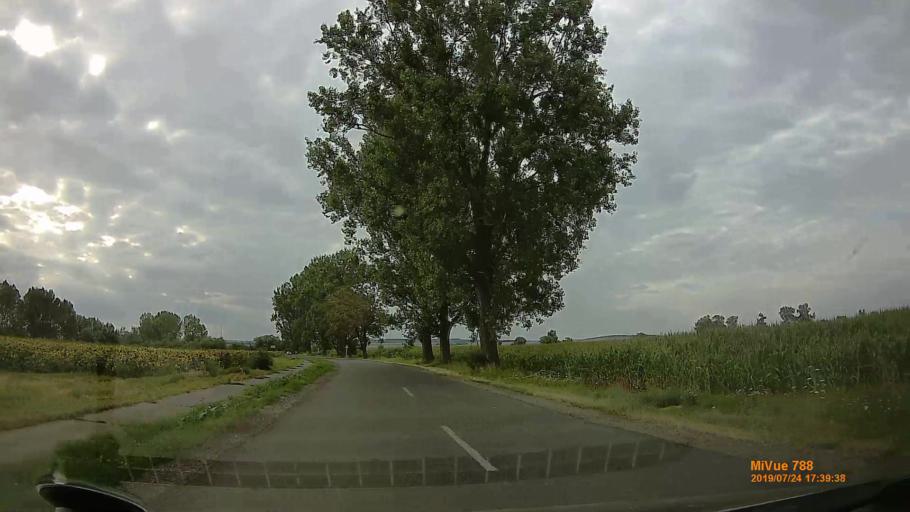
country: HU
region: Borsod-Abauj-Zemplen
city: Encs
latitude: 48.3284
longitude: 21.1416
